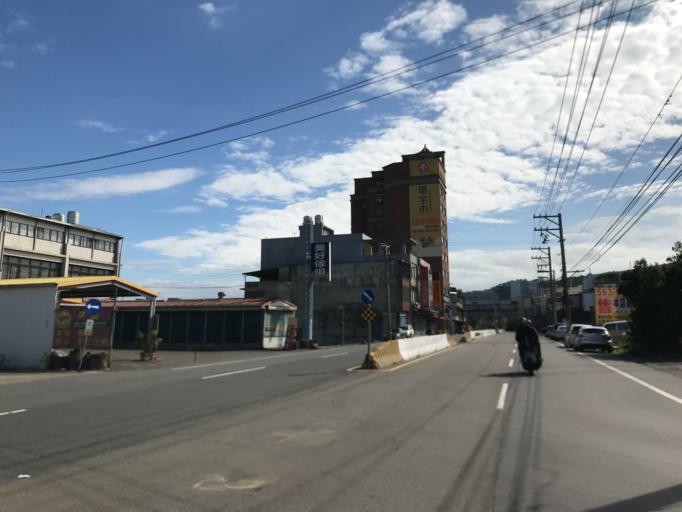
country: TW
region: Taiwan
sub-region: Hsinchu
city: Zhubei
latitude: 24.7783
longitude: 121.0313
